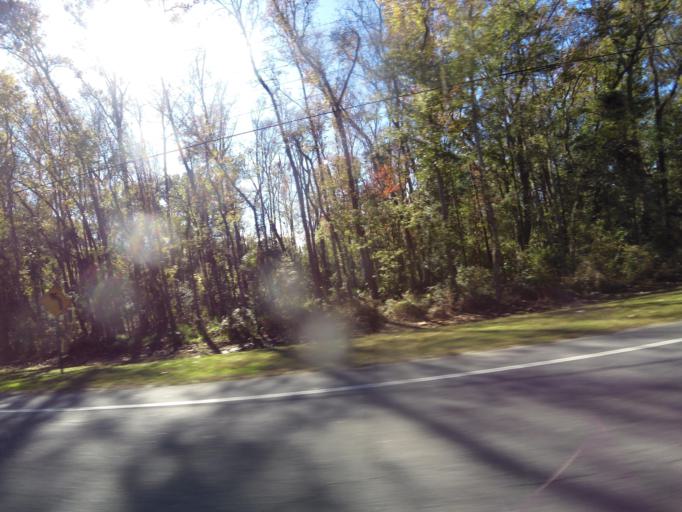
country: US
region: Georgia
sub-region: Chatham County
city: Savannah
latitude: 32.0763
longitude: -81.1261
